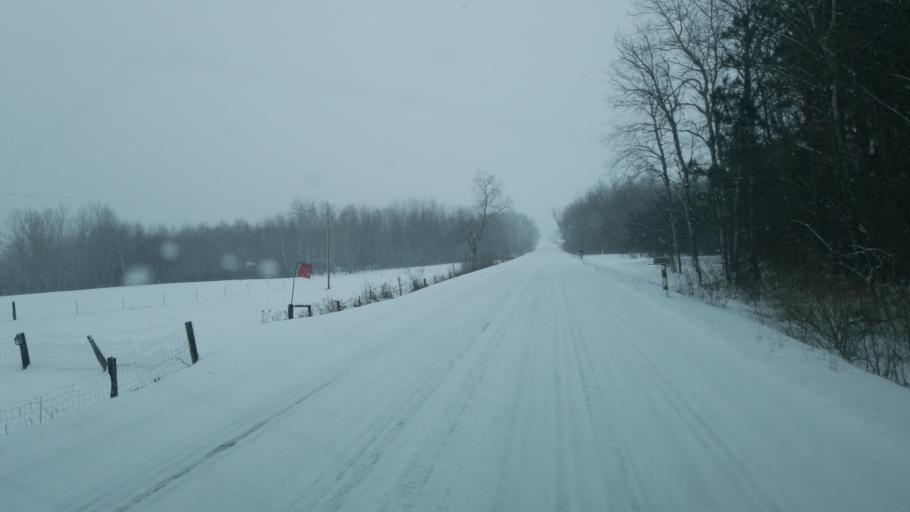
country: US
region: Michigan
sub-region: Mecosta County
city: Canadian Lakes
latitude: 43.5765
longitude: -85.3785
